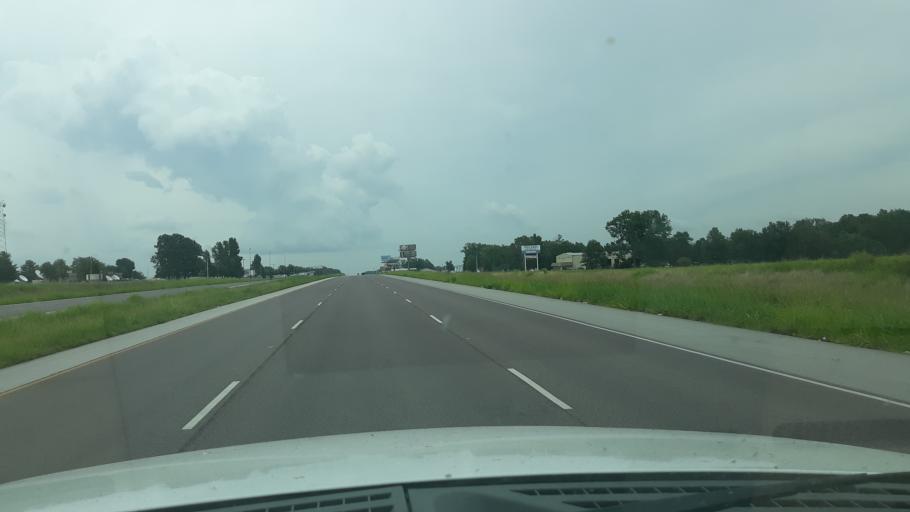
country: US
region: Illinois
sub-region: Williamson County
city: Crainville
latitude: 37.7449
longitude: -89.0579
